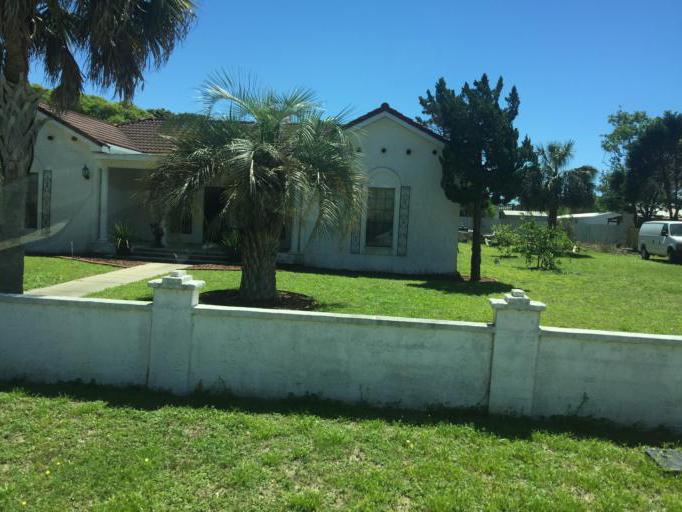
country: US
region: Florida
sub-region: Bay County
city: Laguna Beach
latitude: 30.2413
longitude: -85.9210
